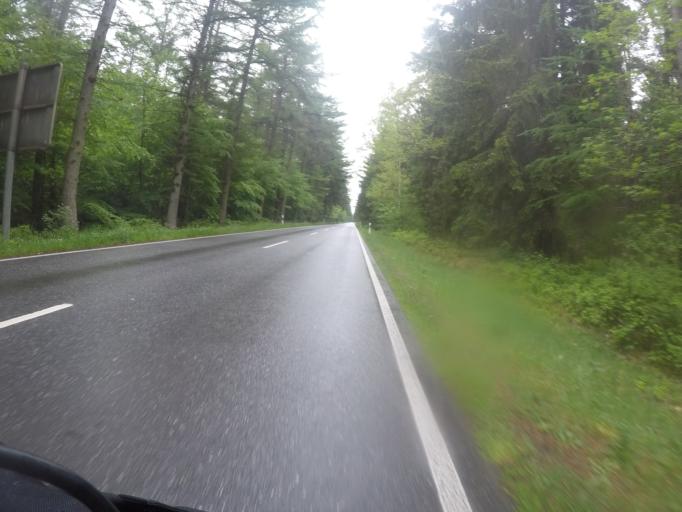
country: DE
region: Schleswig-Holstein
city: Hartenholm
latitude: 53.9221
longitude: 10.0912
